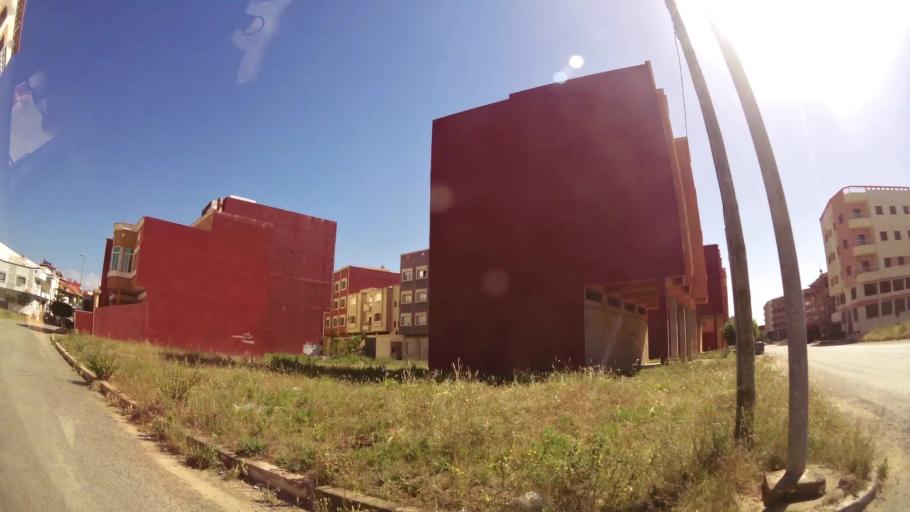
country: MA
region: Oriental
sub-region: Berkane-Taourirt
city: Berkane
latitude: 34.9427
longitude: -2.3300
